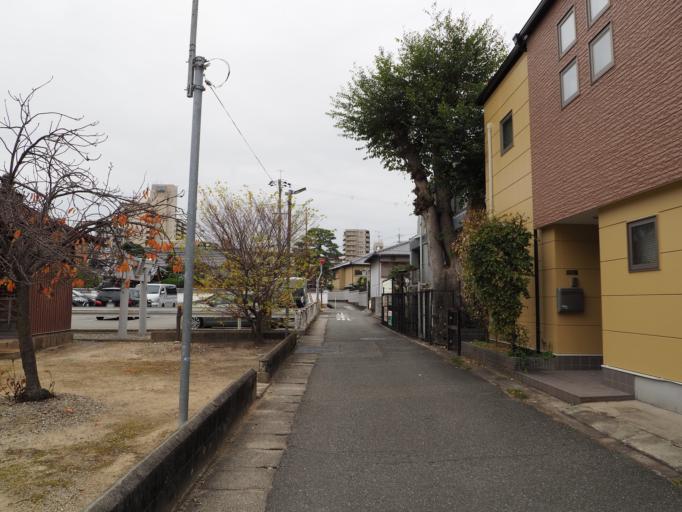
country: JP
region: Hyogo
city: Takarazuka
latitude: 34.7948
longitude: 135.3524
